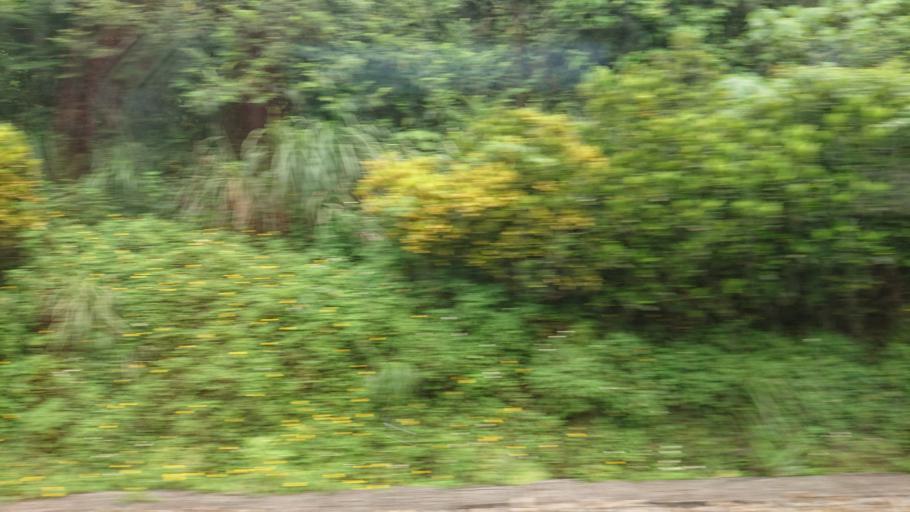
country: TW
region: Taiwan
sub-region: Yilan
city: Yilan
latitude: 24.9465
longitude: 121.9028
